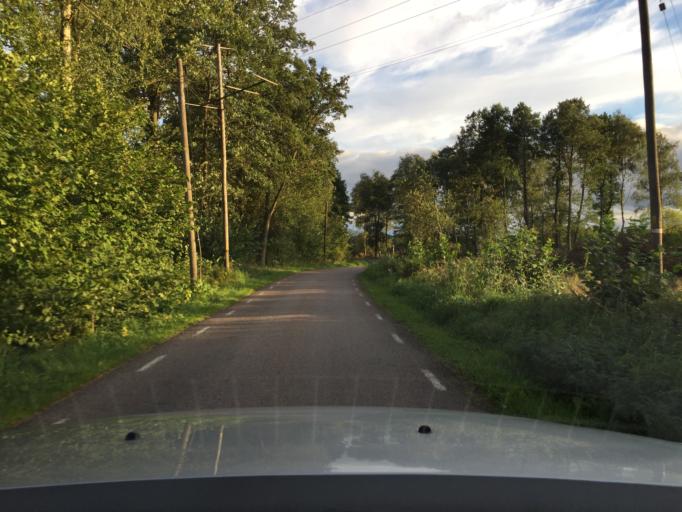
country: SE
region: Skane
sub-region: Hassleholms Kommun
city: Tormestorp
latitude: 56.0095
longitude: 13.7861
